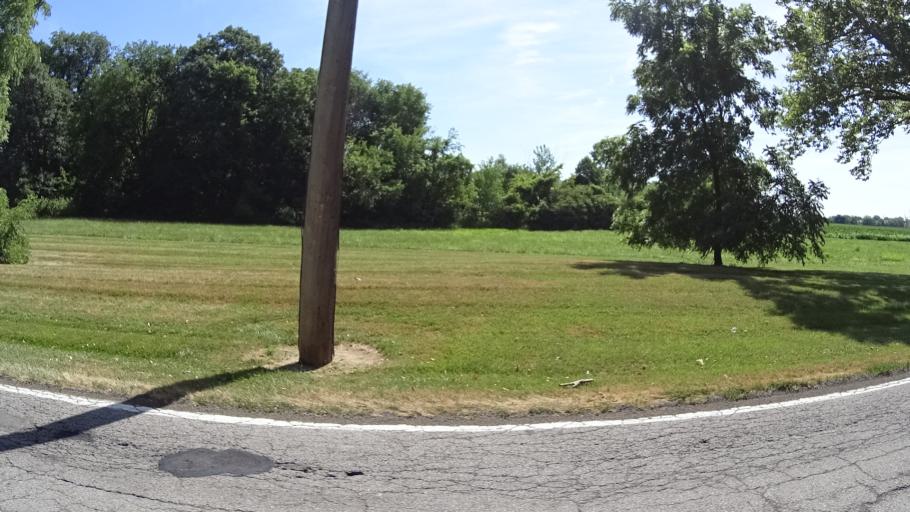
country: US
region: Ohio
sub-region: Erie County
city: Huron
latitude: 41.4209
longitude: -82.6256
